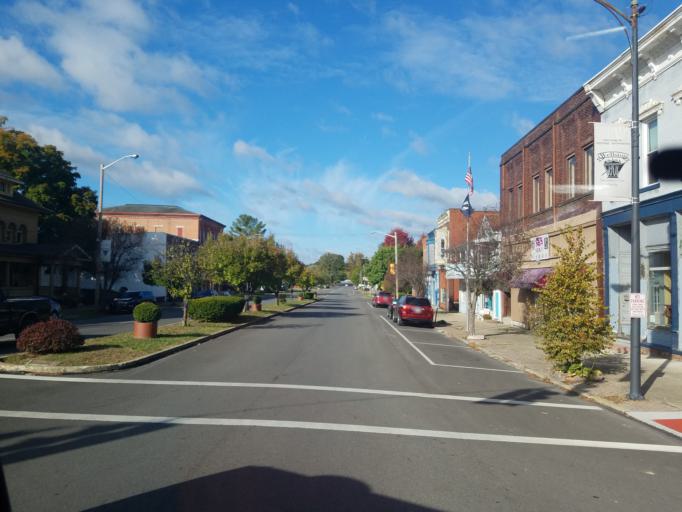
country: US
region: Ohio
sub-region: Jackson County
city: Wellston
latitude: 39.1236
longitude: -82.5342
